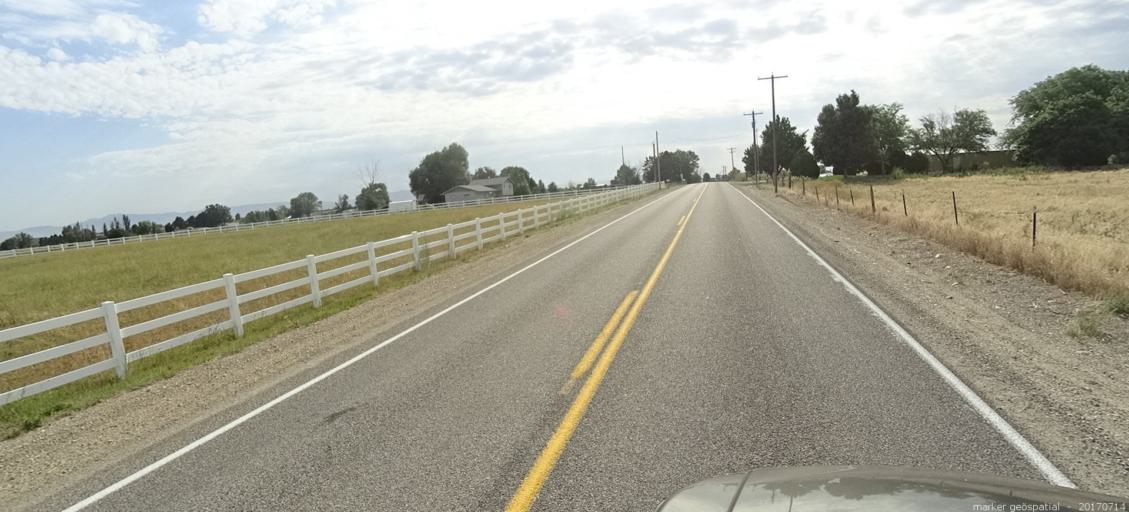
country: US
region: Idaho
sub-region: Ada County
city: Kuna
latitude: 43.4736
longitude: -116.3586
